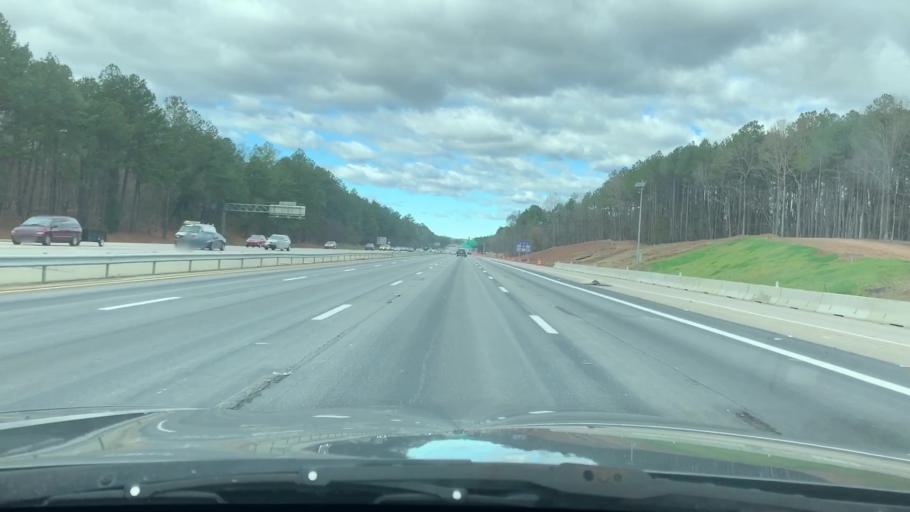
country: US
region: North Carolina
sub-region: Wake County
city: Morrisville
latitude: 35.8524
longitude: -78.8015
